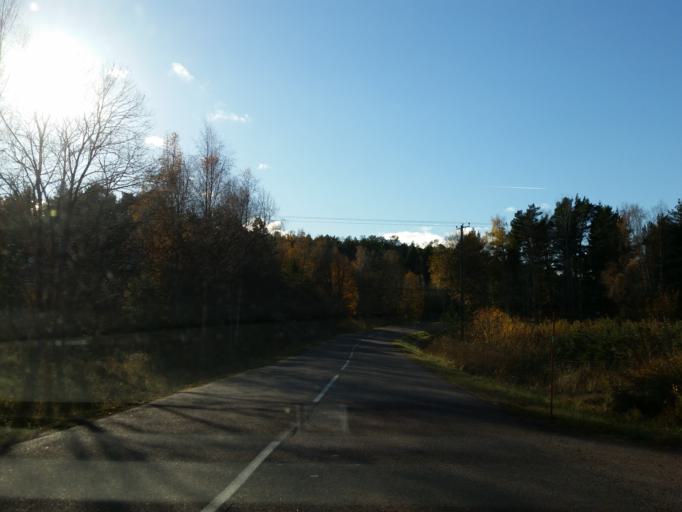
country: AX
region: Alands landsbygd
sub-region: Geta
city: Geta
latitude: 60.3734
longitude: 19.8379
